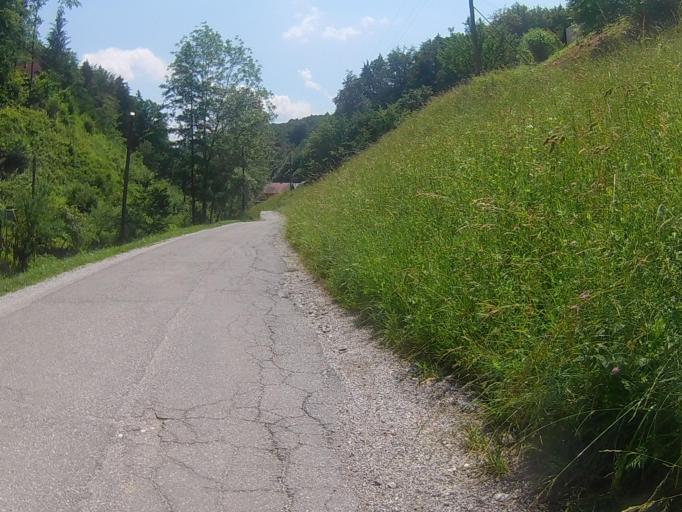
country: SI
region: Maribor
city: Kamnica
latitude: 46.5847
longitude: 15.5965
